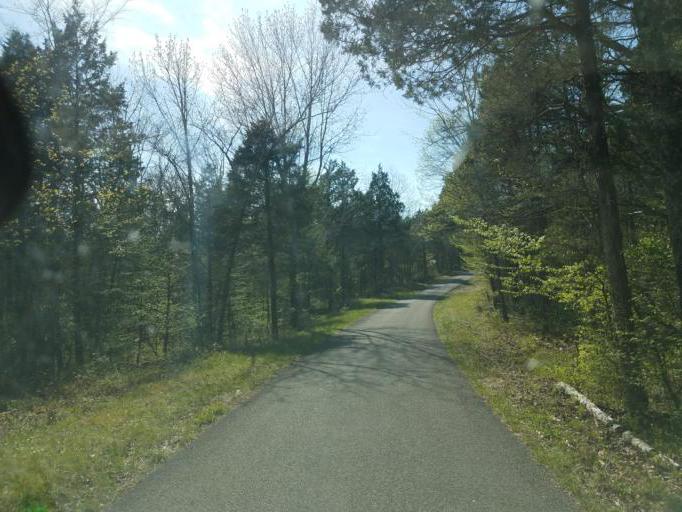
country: US
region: Kentucky
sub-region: Barren County
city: Cave City
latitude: 37.1399
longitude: -85.9644
